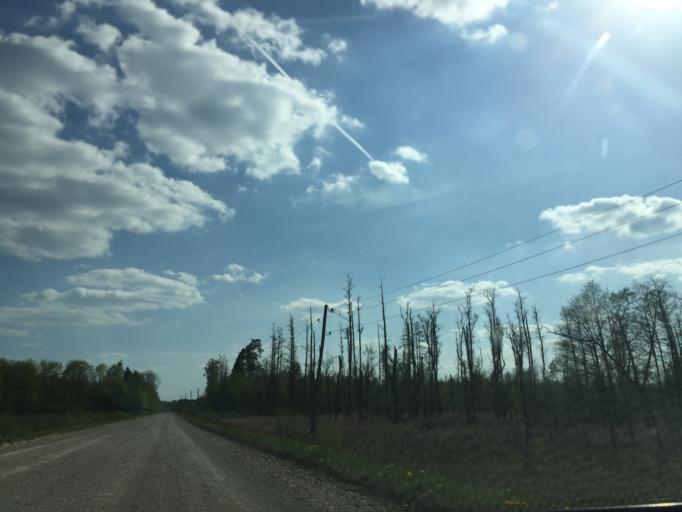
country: LV
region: Vecumnieki
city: Vecumnieki
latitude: 56.5239
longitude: 24.4146
